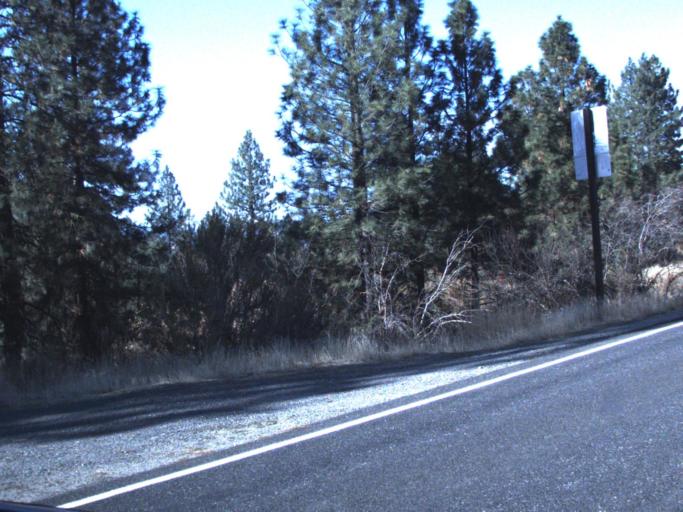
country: US
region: Washington
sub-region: Stevens County
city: Kettle Falls
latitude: 48.1692
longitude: -118.1698
